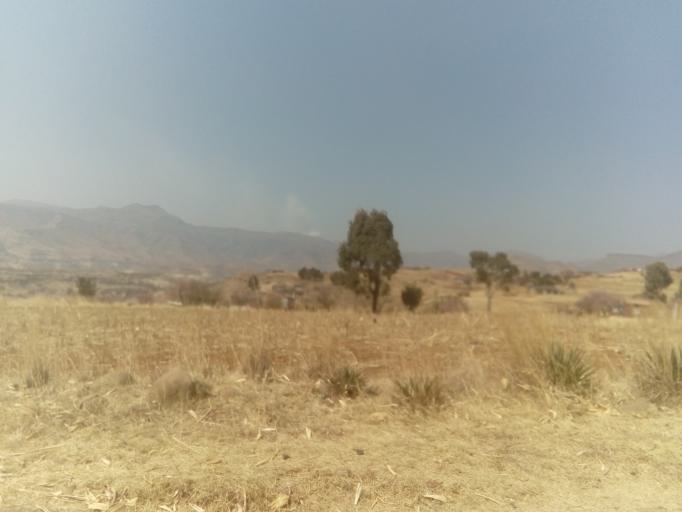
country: LS
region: Leribe
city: Leribe
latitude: -29.1454
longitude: 28.0514
